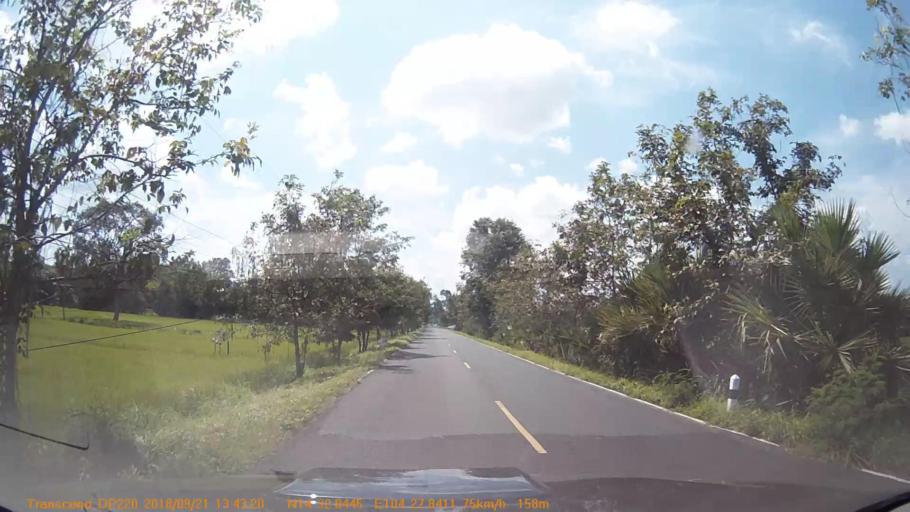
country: TH
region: Sisaket
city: Khun Han
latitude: 14.5475
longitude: 104.4636
